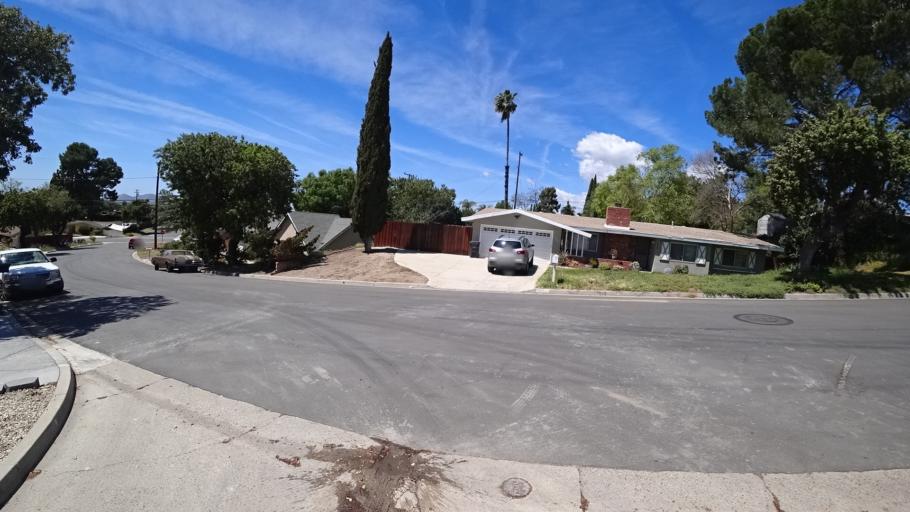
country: US
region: California
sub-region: Ventura County
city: Thousand Oaks
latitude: 34.2153
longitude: -118.8517
